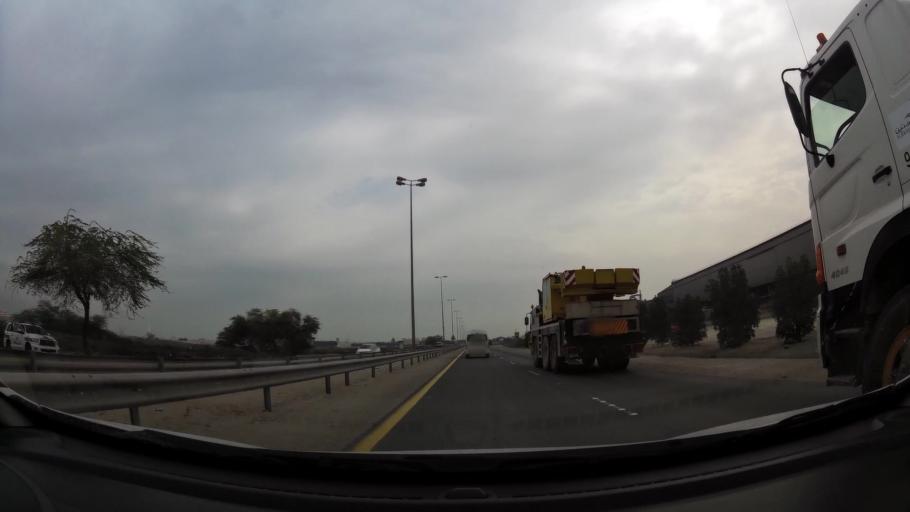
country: BH
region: Northern
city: Sitrah
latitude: 26.0928
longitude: 50.6095
